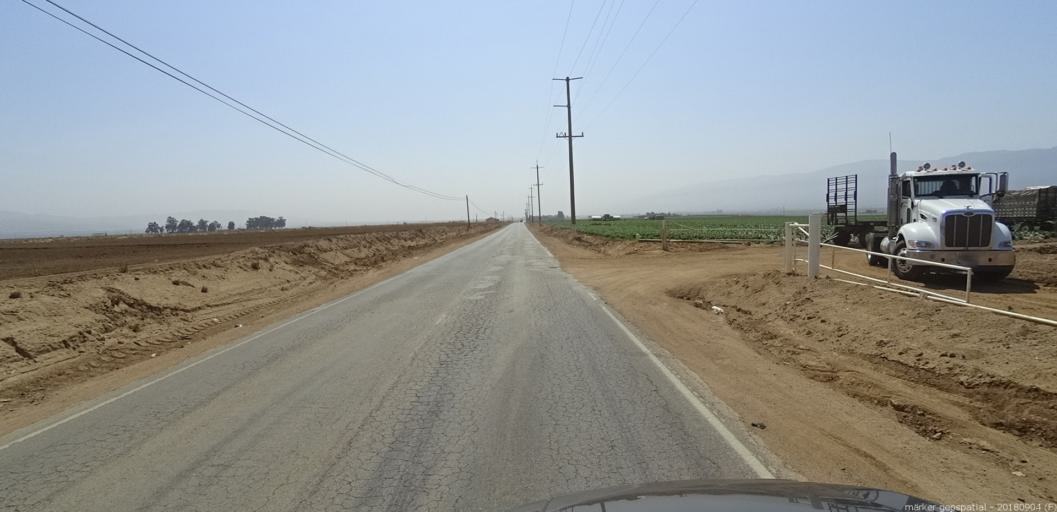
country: US
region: California
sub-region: Monterey County
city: Chualar
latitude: 36.5616
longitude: -121.4821
